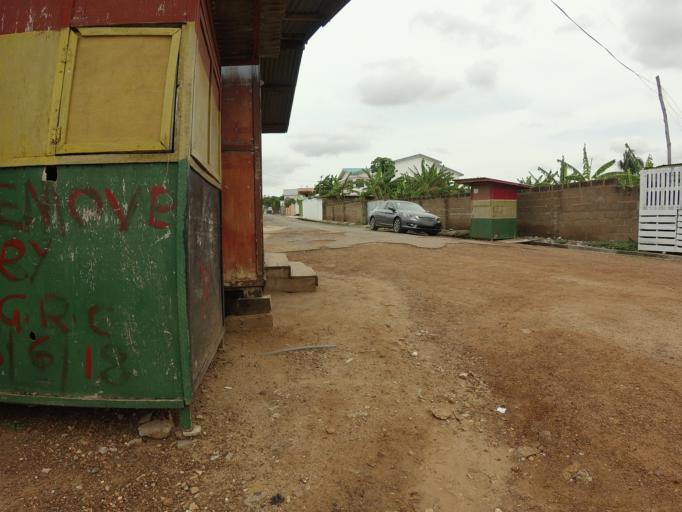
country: GH
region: Greater Accra
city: Dome
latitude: 5.6057
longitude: -0.2229
